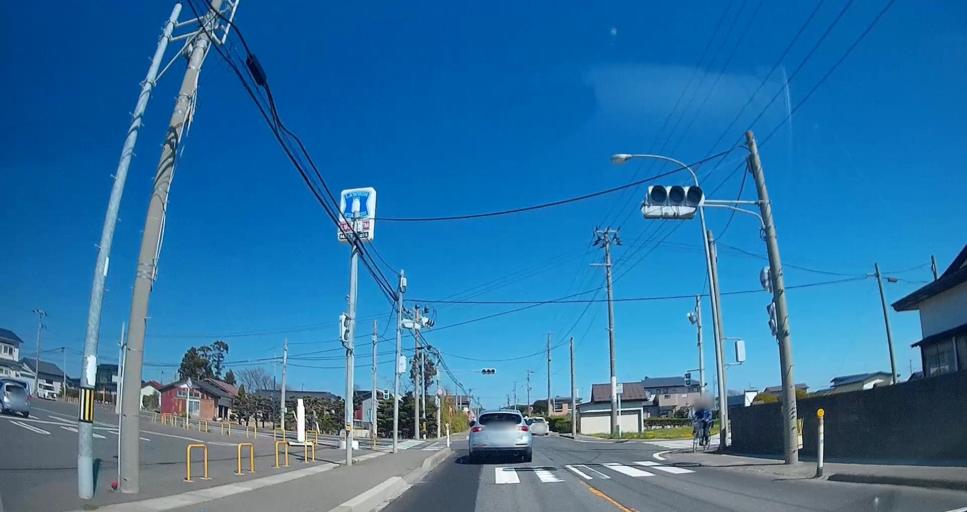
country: JP
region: Aomori
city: Misawa
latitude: 40.6416
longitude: 141.4415
